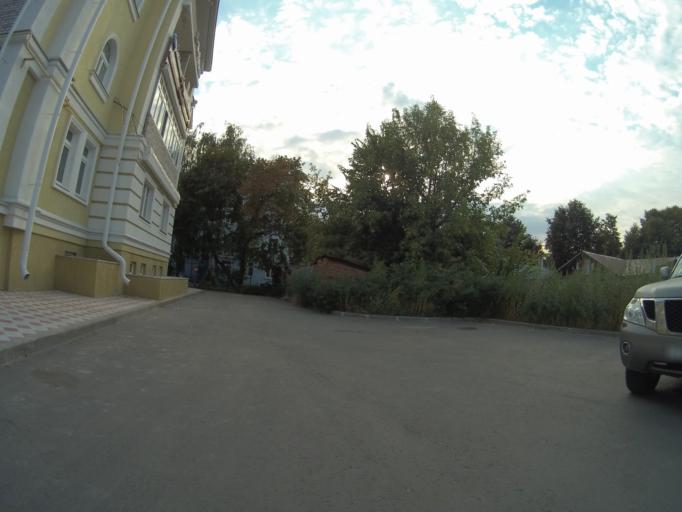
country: RU
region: Vladimir
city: Vladimir
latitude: 56.1337
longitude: 40.4176
